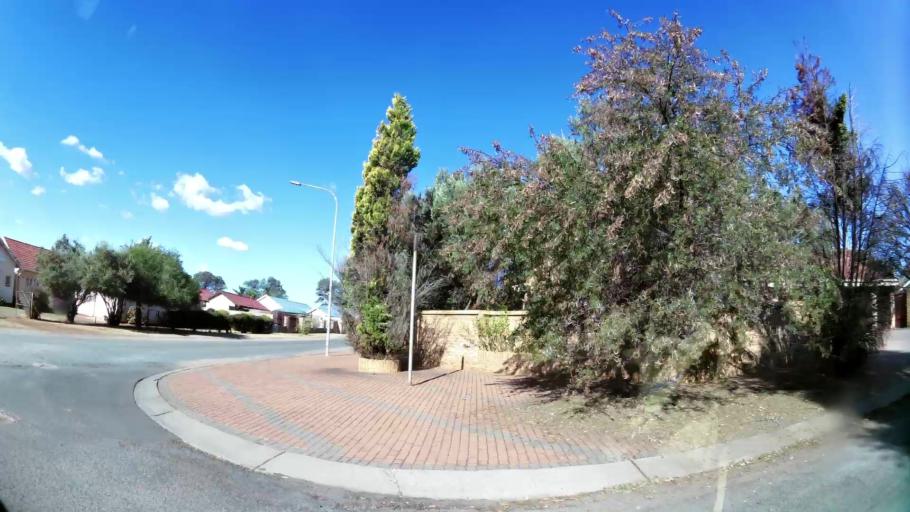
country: ZA
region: Gauteng
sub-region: West Rand District Municipality
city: Carletonville
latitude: -26.3641
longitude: 27.3699
